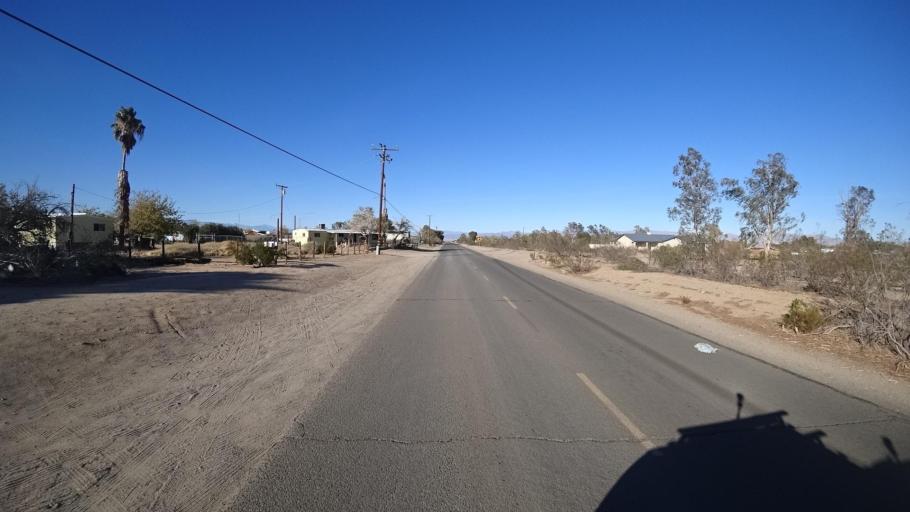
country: US
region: California
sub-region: Kern County
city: Ridgecrest
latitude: 35.6422
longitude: -117.7056
